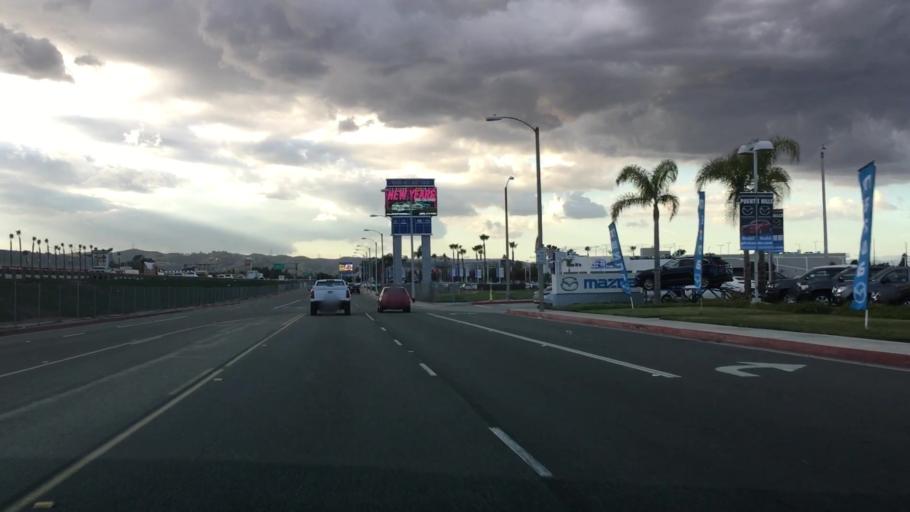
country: US
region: California
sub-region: Los Angeles County
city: South San Jose Hills
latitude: 33.9958
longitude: -117.9188
